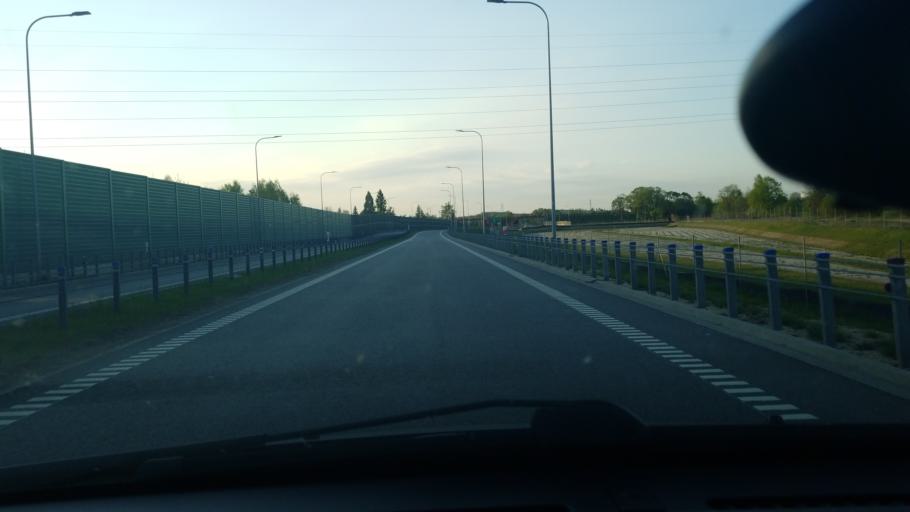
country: PL
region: Silesian Voivodeship
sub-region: Powiat czestochowski
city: Blachownia
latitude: 50.7812
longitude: 19.0114
